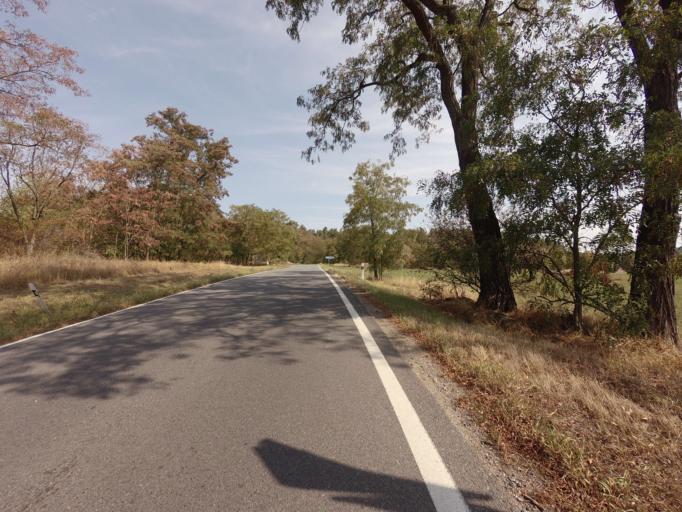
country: CZ
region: Central Bohemia
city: Petrovice
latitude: 49.5647
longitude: 14.3618
